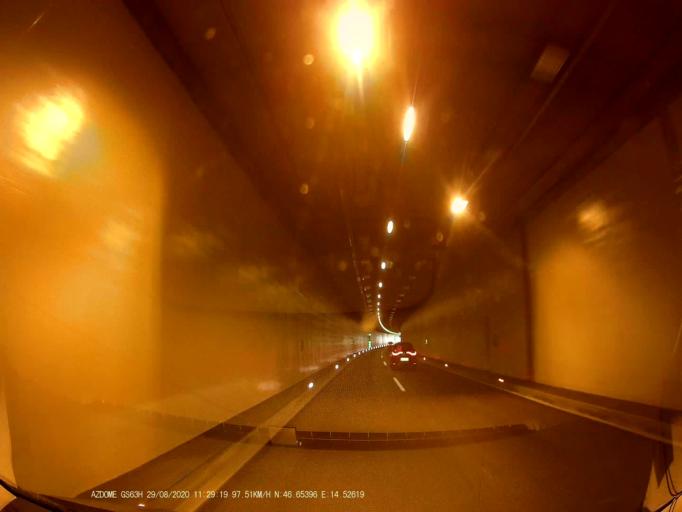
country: AT
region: Carinthia
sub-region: Politischer Bezirk Klagenfurt Land
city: Poggersdorf
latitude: 46.6544
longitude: 14.5277
